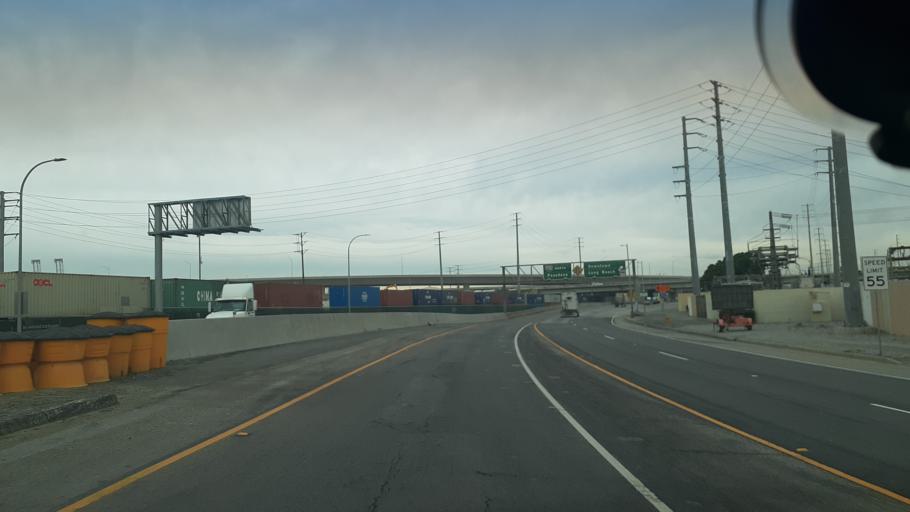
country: US
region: California
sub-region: Los Angeles County
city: Long Beach
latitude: 33.7643
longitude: -118.2069
